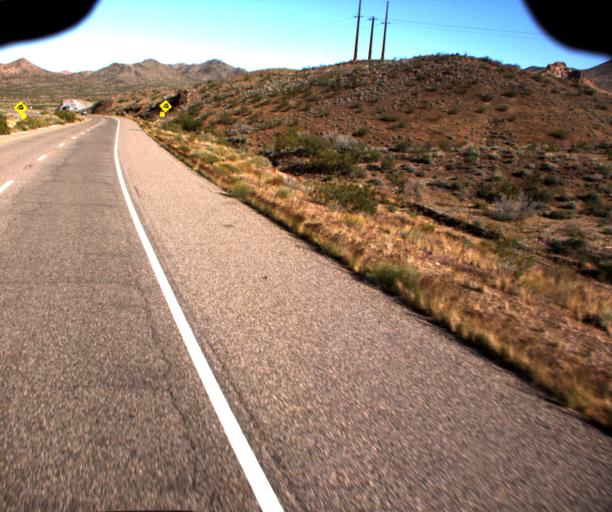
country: US
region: Arizona
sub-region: Mohave County
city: Bullhead City
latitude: 35.1951
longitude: -114.4123
